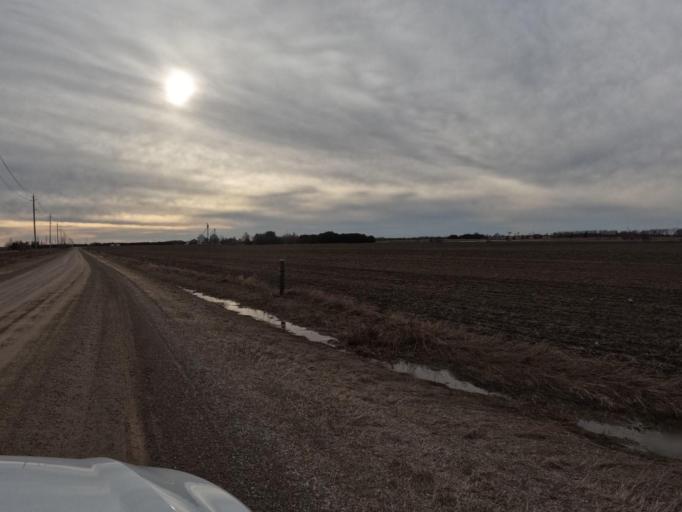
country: CA
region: Ontario
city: Orangeville
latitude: 43.9198
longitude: -80.2299
